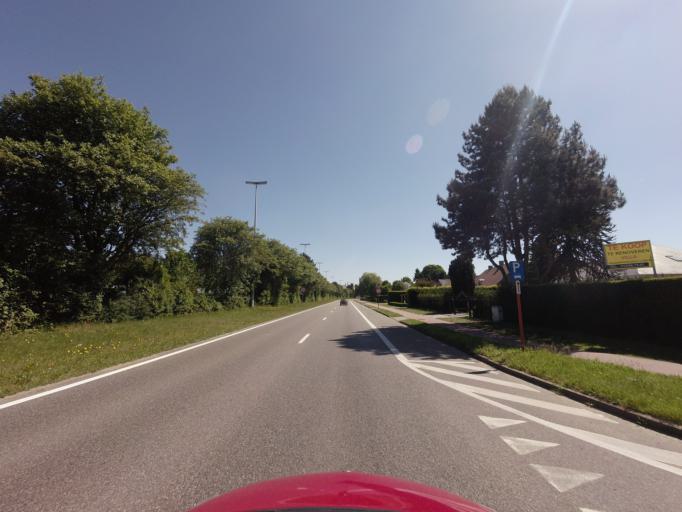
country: BE
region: Flanders
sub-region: Provincie Antwerpen
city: Oud-Turnhout
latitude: 51.3251
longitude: 4.9666
